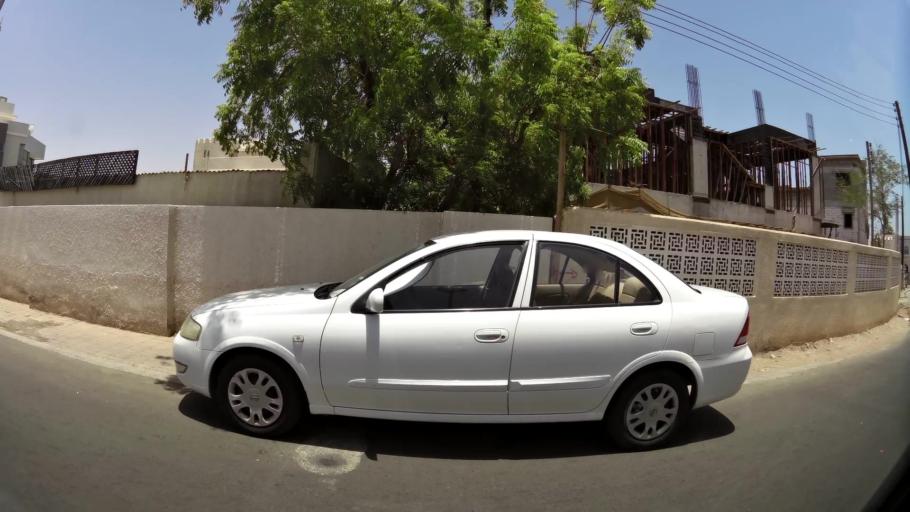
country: OM
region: Muhafazat Masqat
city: Bawshar
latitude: 23.6003
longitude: 58.4526
